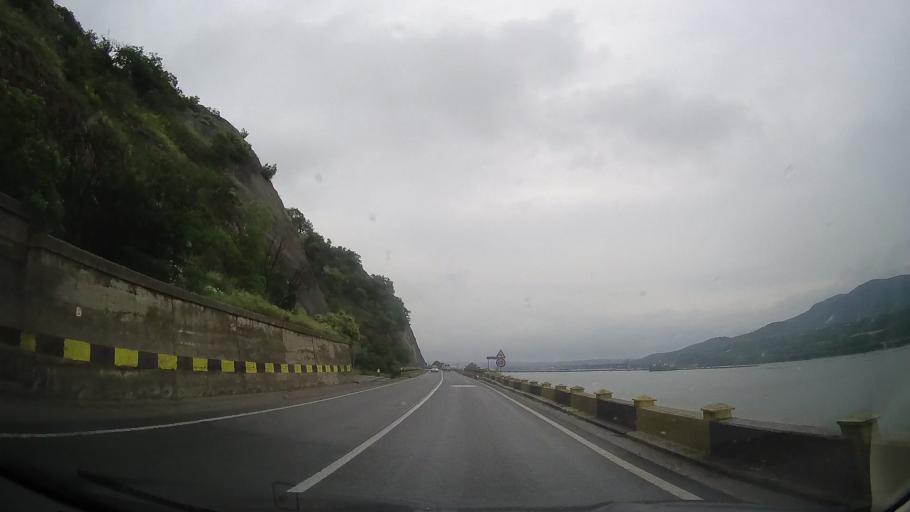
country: RO
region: Mehedinti
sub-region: Municipiul Drobeta-Turnu Severin
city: Gura Vaii
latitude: 44.6857
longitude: 22.5159
